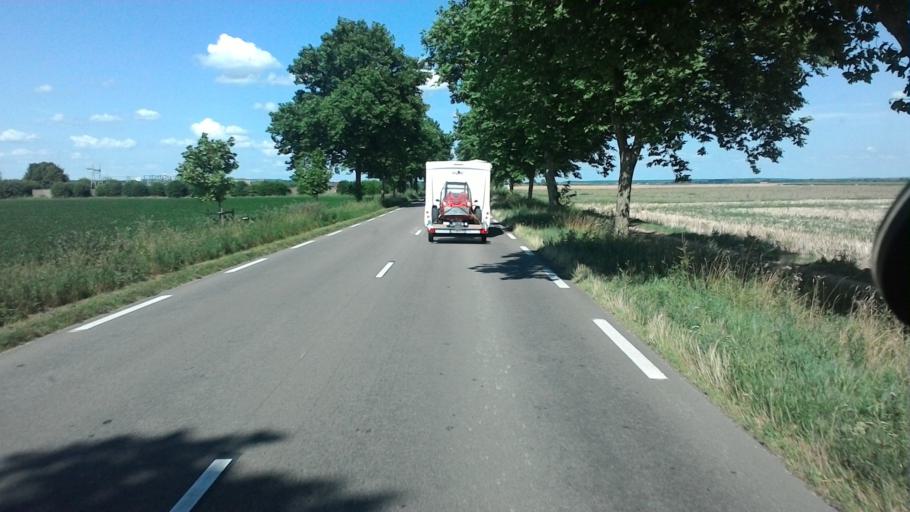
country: FR
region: Franche-Comte
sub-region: Departement du Jura
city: Tavaux
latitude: 47.0203
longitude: 5.3829
